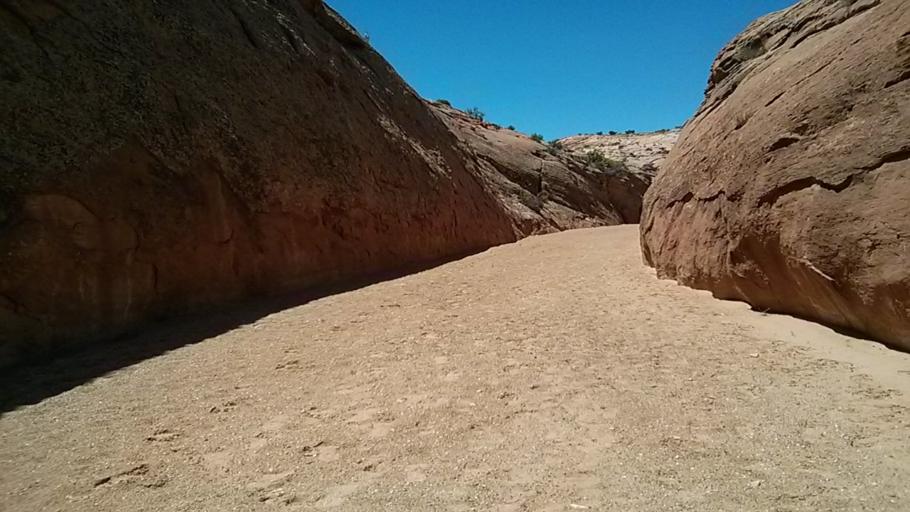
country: US
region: Arizona
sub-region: Coconino County
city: Page
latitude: 37.4796
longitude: -111.2091
